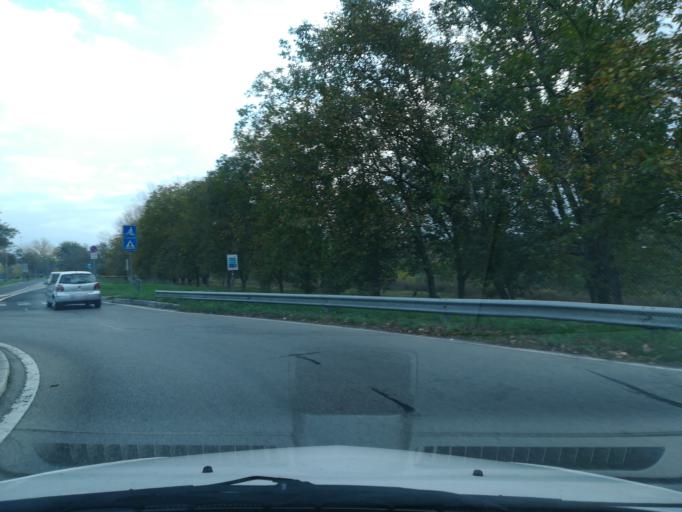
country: IT
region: Emilia-Romagna
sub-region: Provincia di Bologna
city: Imola
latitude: 44.3457
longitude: 11.7181
